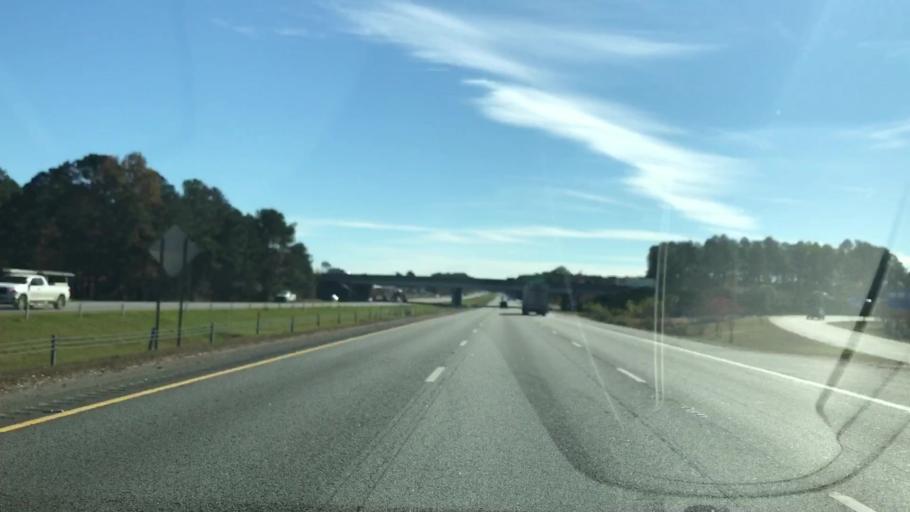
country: US
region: South Carolina
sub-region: Berkeley County
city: Sangaree
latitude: 33.0400
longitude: -80.1507
